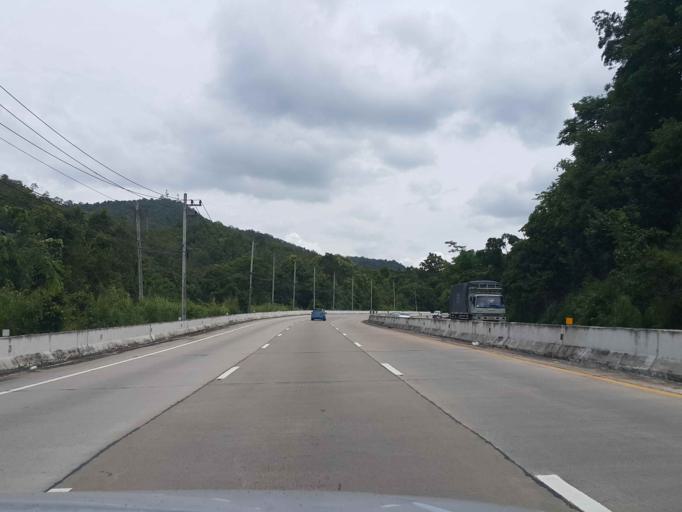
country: TH
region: Lamphun
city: Mae Tha
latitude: 18.4465
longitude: 99.2044
